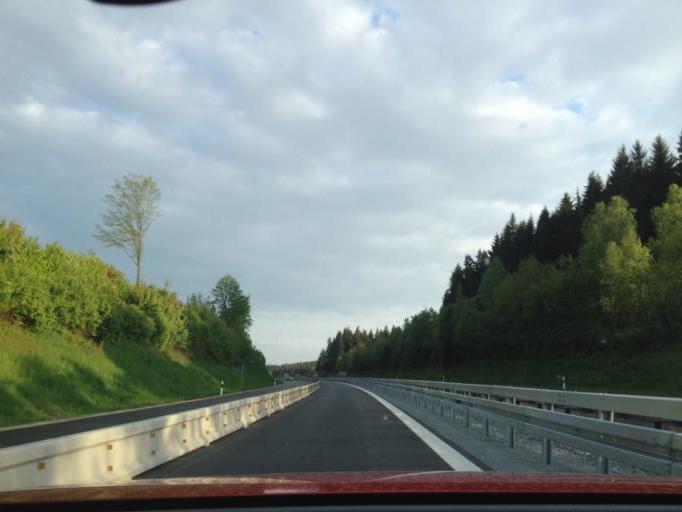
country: DE
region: Bavaria
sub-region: Upper Palatinate
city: Windischeschenbach
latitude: 49.7683
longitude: 12.1521
